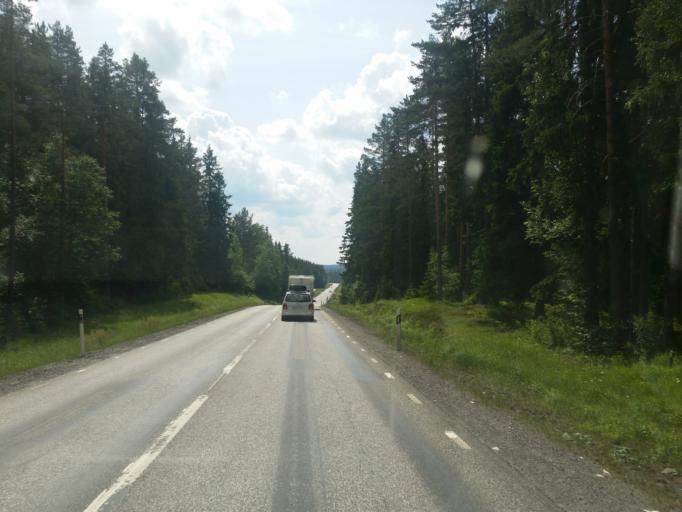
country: SE
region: OErebro
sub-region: Ljusnarsbergs Kommun
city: Kopparberg
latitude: 59.9056
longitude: 15.0210
